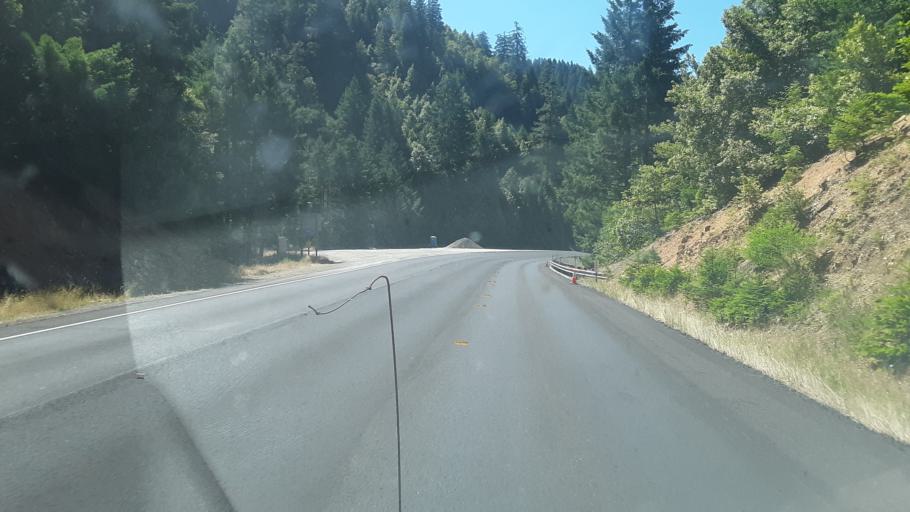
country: US
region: Oregon
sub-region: Josephine County
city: Cave Junction
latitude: 41.9562
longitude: -123.7438
